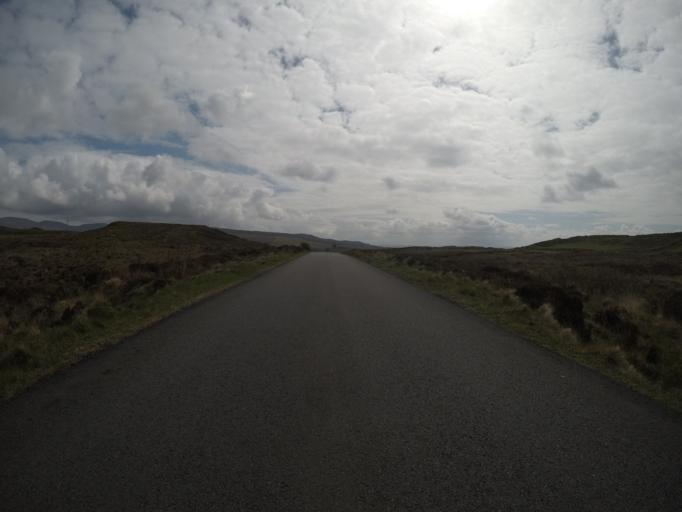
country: GB
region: Scotland
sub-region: Highland
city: Portree
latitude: 57.5959
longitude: -6.3746
